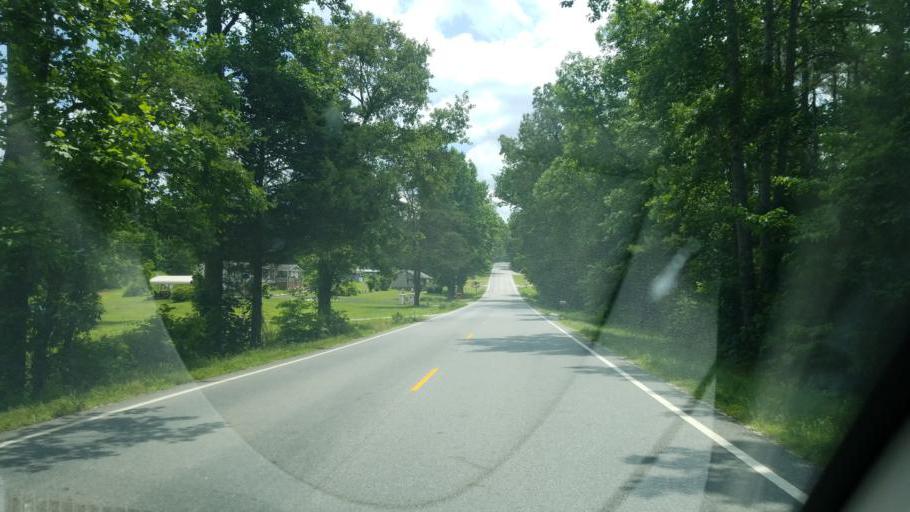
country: US
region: Virginia
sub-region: Nelson County
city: Lovingston
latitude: 37.5686
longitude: -78.8517
